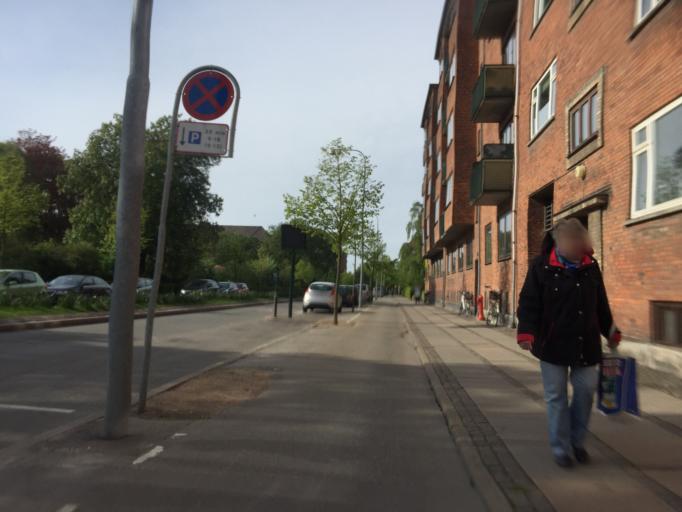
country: DK
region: Capital Region
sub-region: Kobenhavn
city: Vanlose
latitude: 55.6814
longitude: 12.5107
